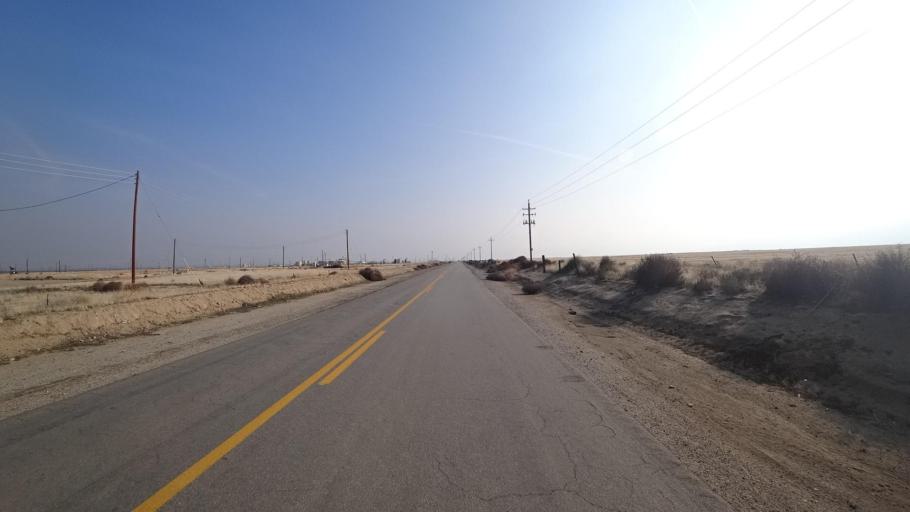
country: US
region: California
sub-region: Kern County
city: Lebec
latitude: 34.9845
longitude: -118.9344
